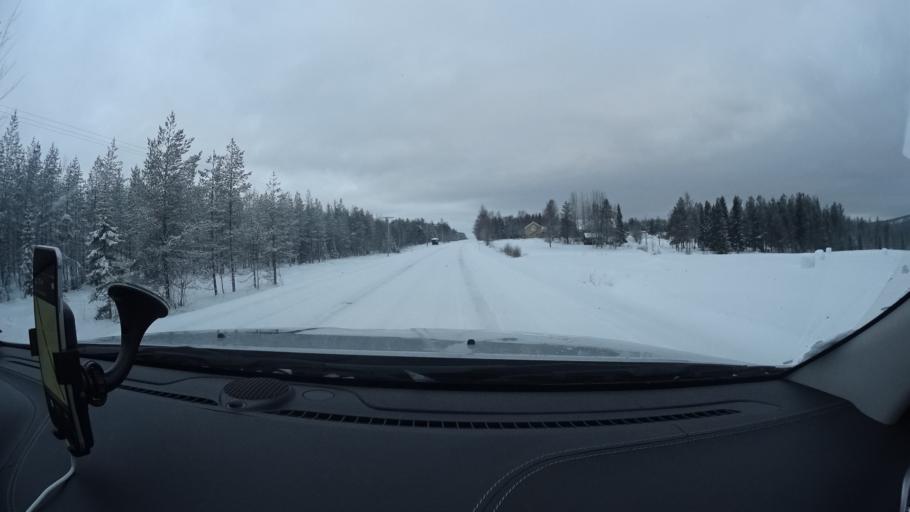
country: FI
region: Lapland
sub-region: Itae-Lappi
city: Kemijaervi
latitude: 66.2942
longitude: 27.1356
